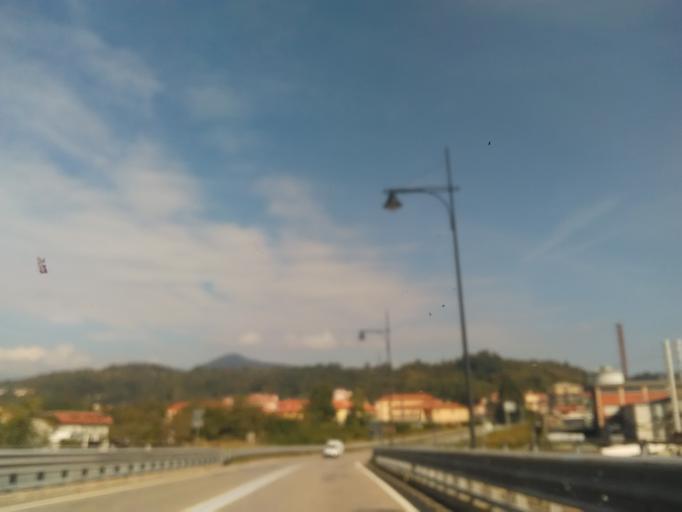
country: IT
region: Piedmont
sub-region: Provincia di Vercelli
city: Borgosesia
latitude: 45.7142
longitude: 8.2678
